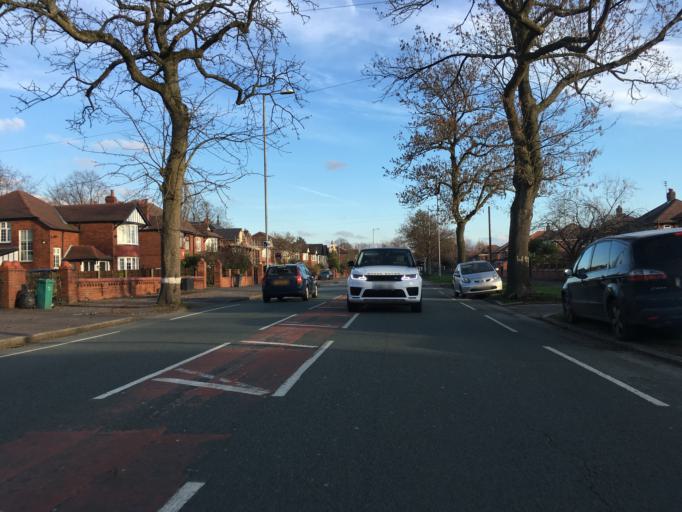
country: GB
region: England
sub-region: Manchester
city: Chorlton cum Hardy
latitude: 53.4433
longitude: -2.2597
